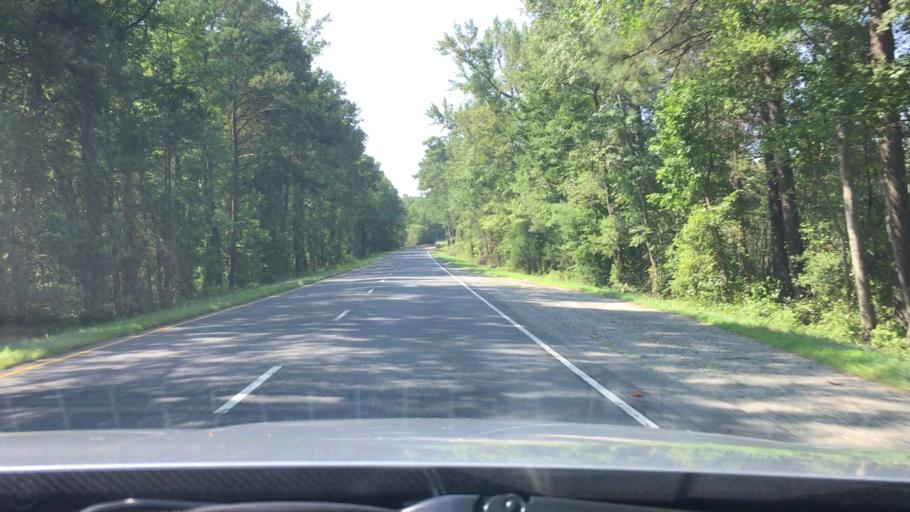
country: US
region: Virginia
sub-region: Caroline County
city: Bowling Green
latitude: 37.9708
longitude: -77.4278
